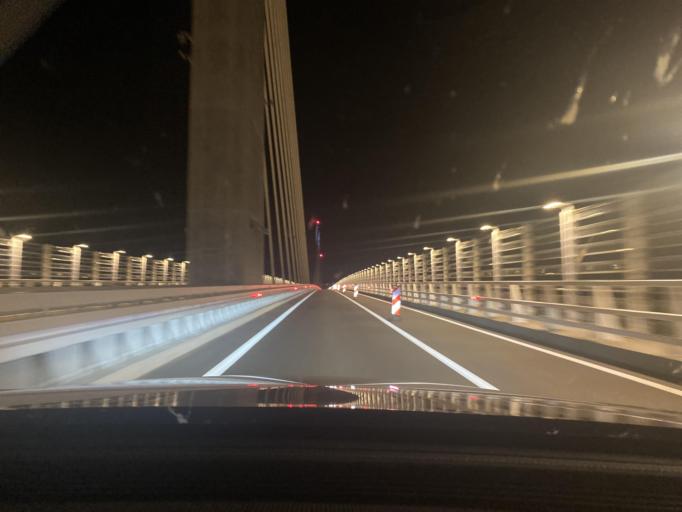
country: BA
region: Federation of Bosnia and Herzegovina
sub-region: Hercegovacko-Bosanski Kanton
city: Neum
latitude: 42.9310
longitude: 17.5352
